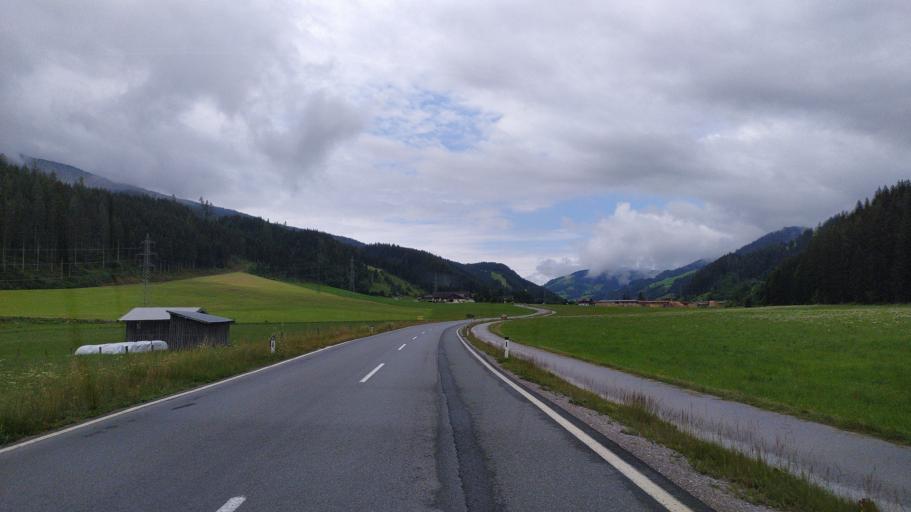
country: AT
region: Salzburg
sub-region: Politischer Bezirk Sankt Johann im Pongau
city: Flachau
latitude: 47.3613
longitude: 13.3774
